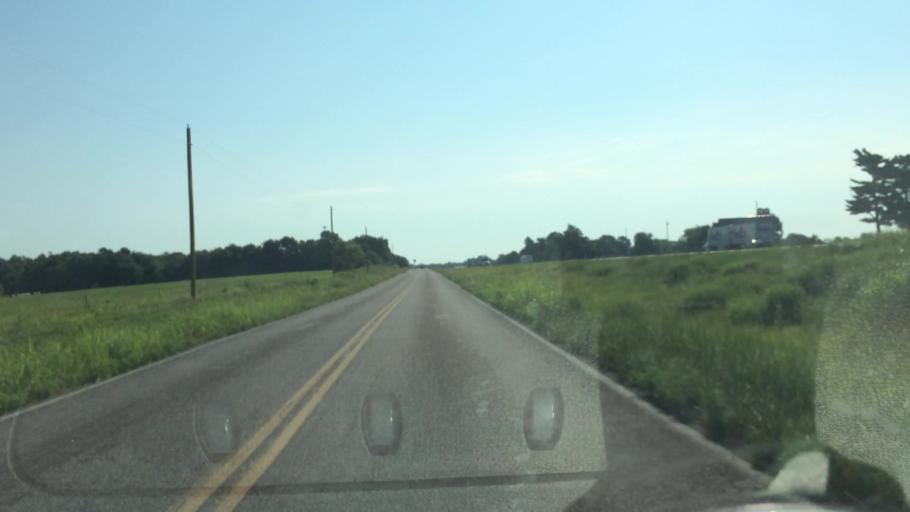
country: US
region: Missouri
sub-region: Greene County
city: Strafford
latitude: 37.2610
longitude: -93.1527
